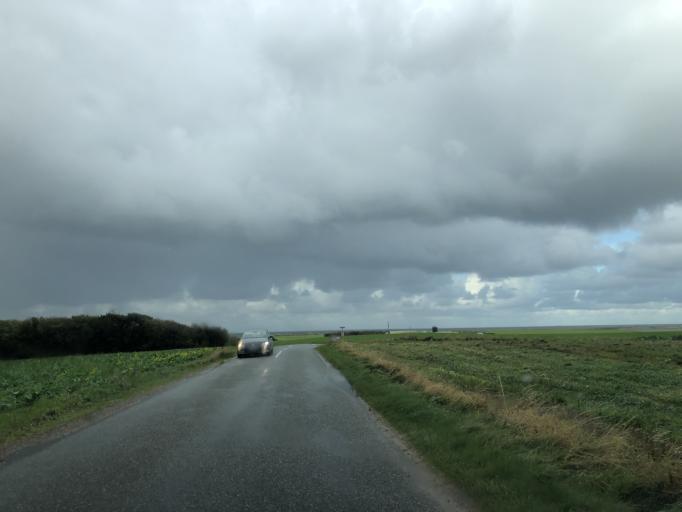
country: DK
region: Central Jutland
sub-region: Lemvig Kommune
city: Harboore
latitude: 56.5465
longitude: 8.1587
